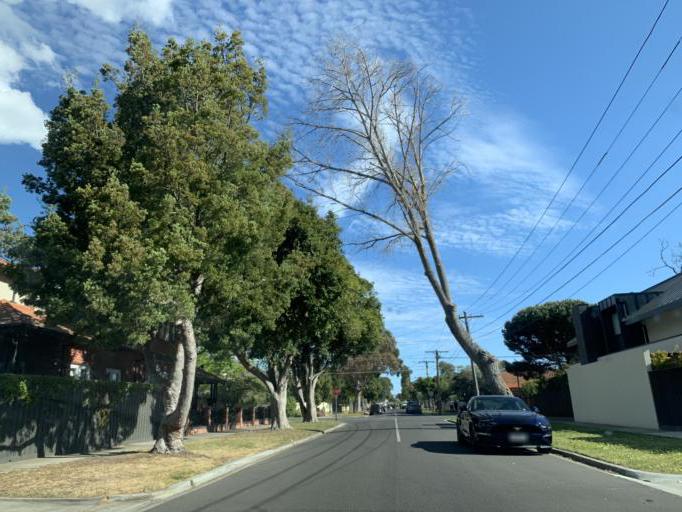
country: AU
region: Victoria
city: Hampton
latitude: -37.9511
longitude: 145.0149
